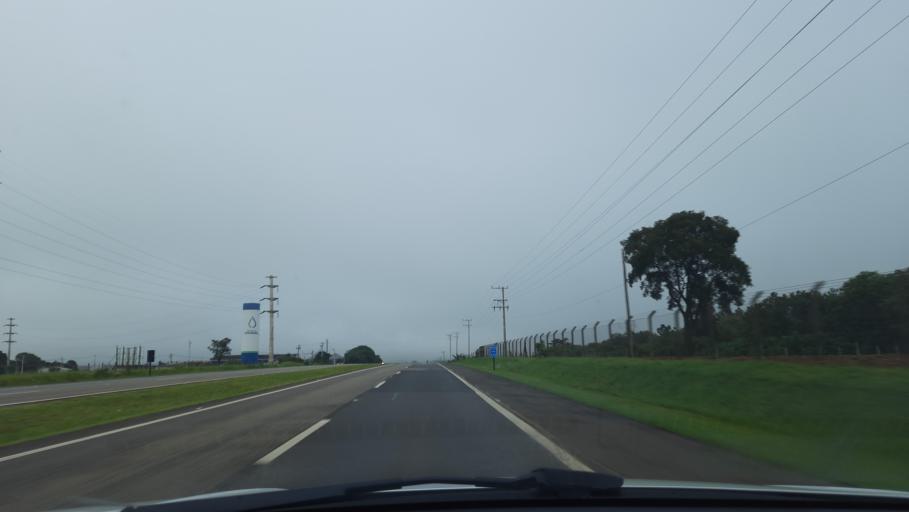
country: BR
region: Sao Paulo
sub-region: Casa Branca
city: Casa Branca
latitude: -21.7593
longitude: -47.0704
